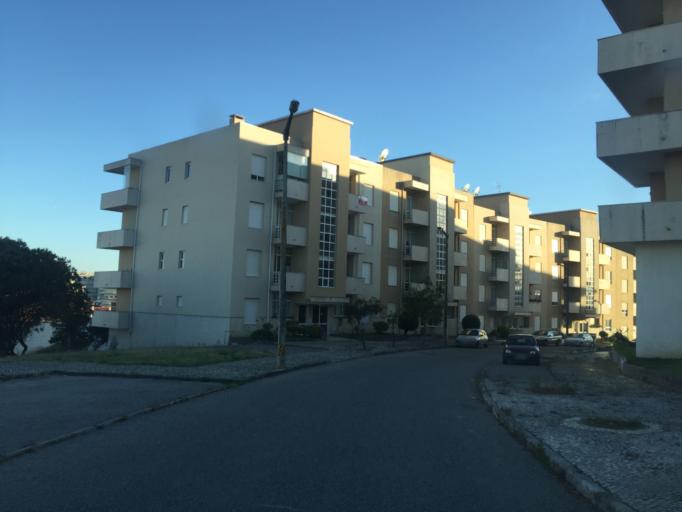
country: PT
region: Coimbra
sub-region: Figueira da Foz
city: Figueira da Foz
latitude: 40.1583
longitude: -8.8663
